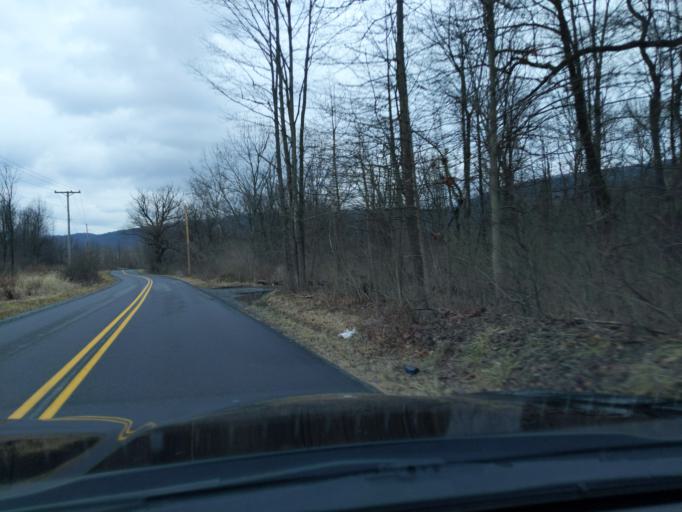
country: US
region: Pennsylvania
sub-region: Blair County
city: Tipton
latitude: 40.6278
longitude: -78.3085
